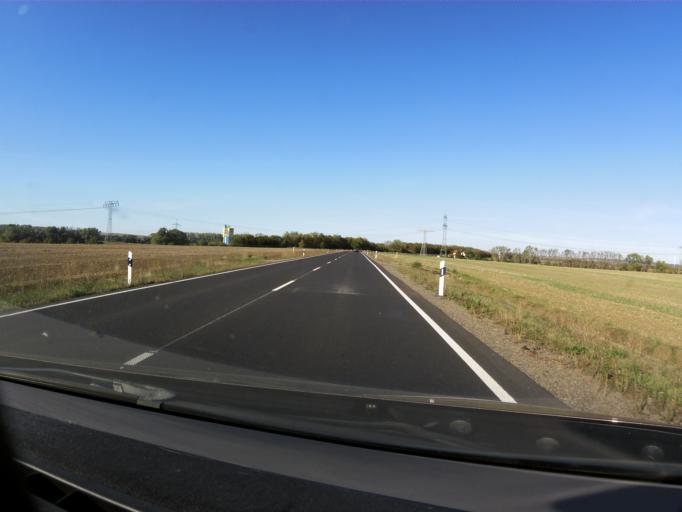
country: DE
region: Saxony-Anhalt
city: Quedlinburg
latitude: 51.7944
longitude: 11.1839
